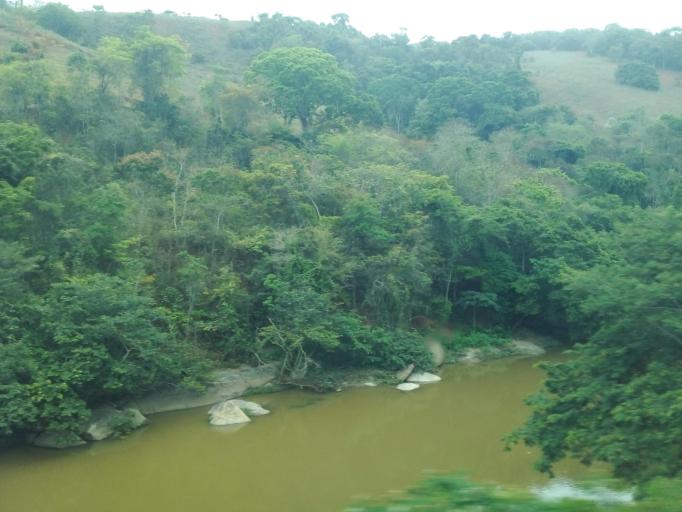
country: BR
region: Minas Gerais
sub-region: Nova Era
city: Nova Era
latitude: -19.7235
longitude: -42.9694
